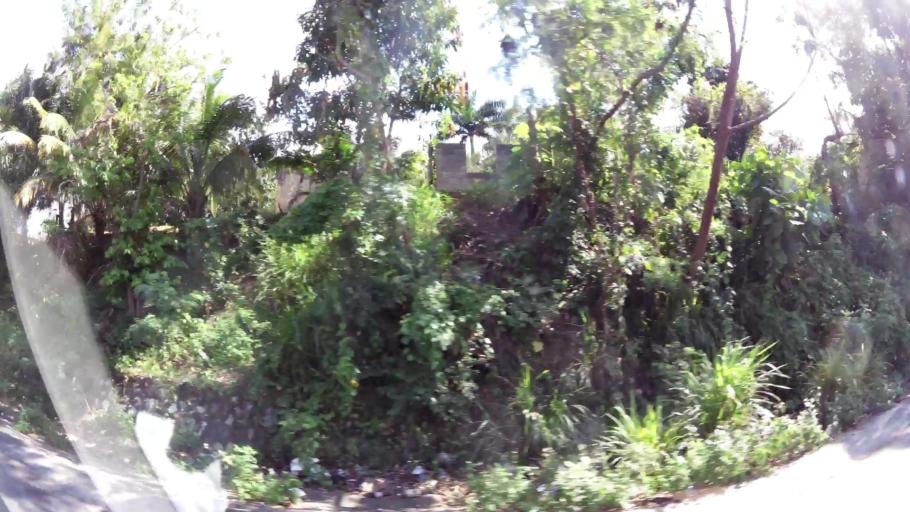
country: DO
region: San Cristobal
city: Bajos de Haina
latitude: 18.4274
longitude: -70.0621
